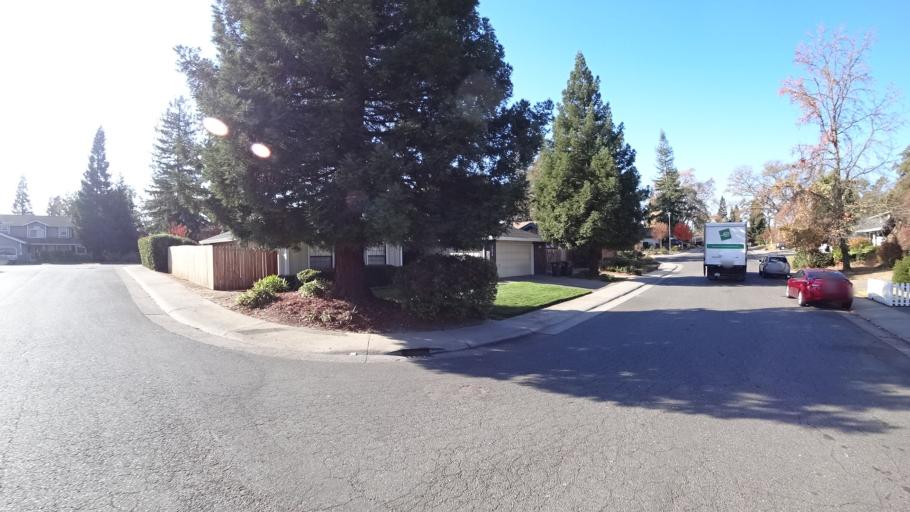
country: US
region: California
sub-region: Sacramento County
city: Citrus Heights
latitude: 38.6852
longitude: -121.2815
